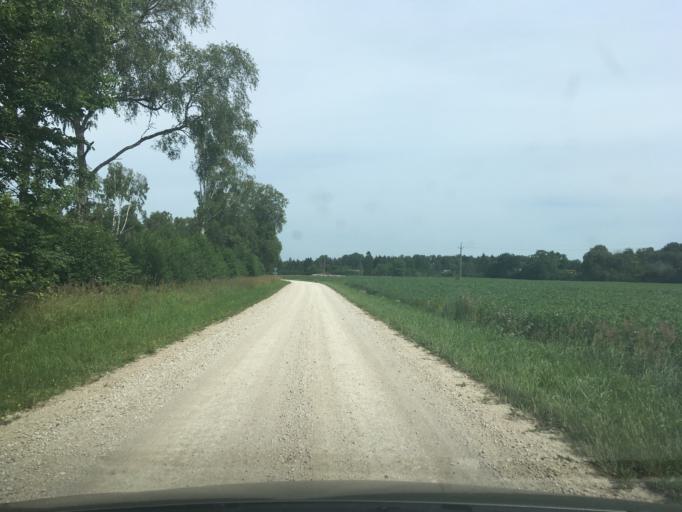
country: EE
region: Raplamaa
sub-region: Maerjamaa vald
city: Marjamaa
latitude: 58.9413
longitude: 24.5531
